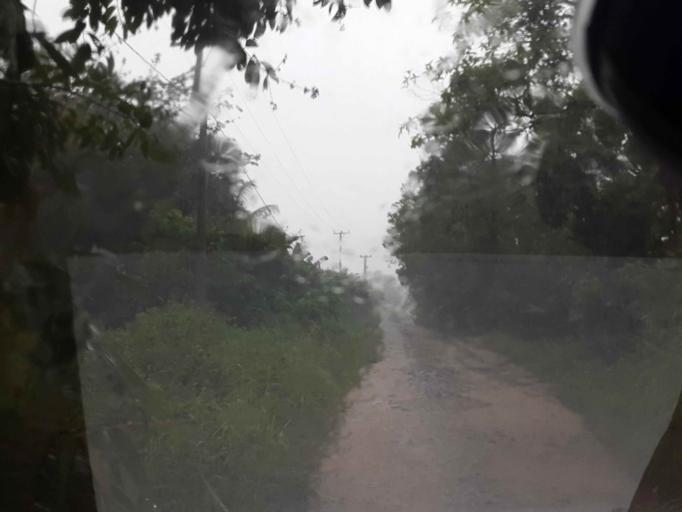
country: ID
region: Lampung
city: Kedaton
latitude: -5.3921
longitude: 105.3312
